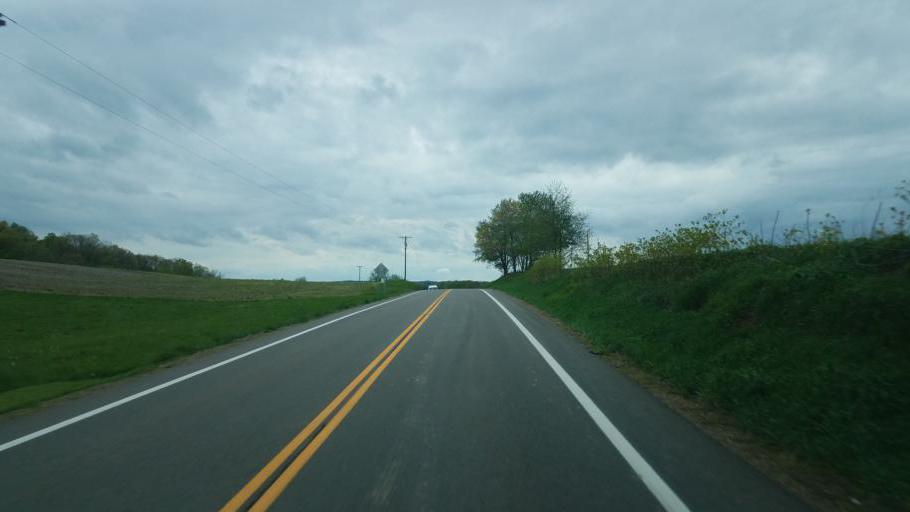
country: US
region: Ohio
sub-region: Sandusky County
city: Bellville
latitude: 40.6207
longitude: -82.4004
